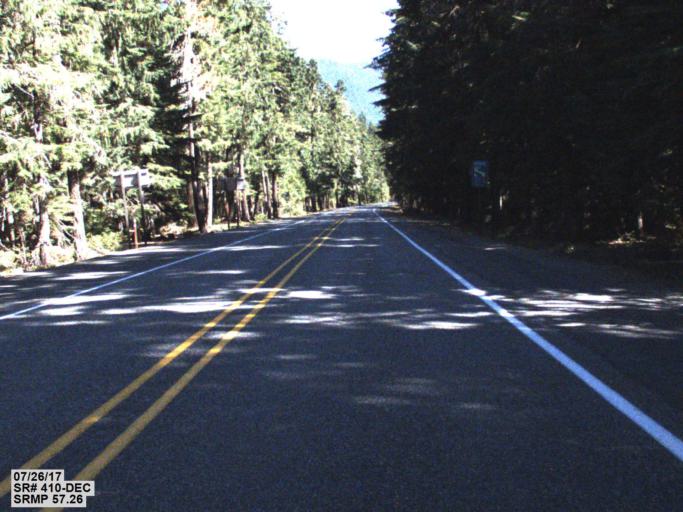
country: US
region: Washington
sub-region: King County
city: Enumclaw
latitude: 46.9832
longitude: -121.5355
